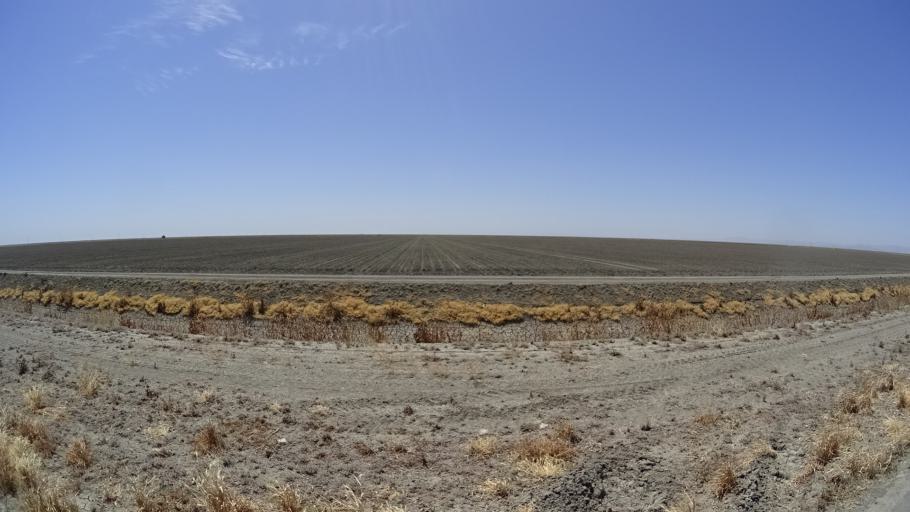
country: US
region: California
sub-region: Kings County
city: Stratford
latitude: 36.1233
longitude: -119.7230
